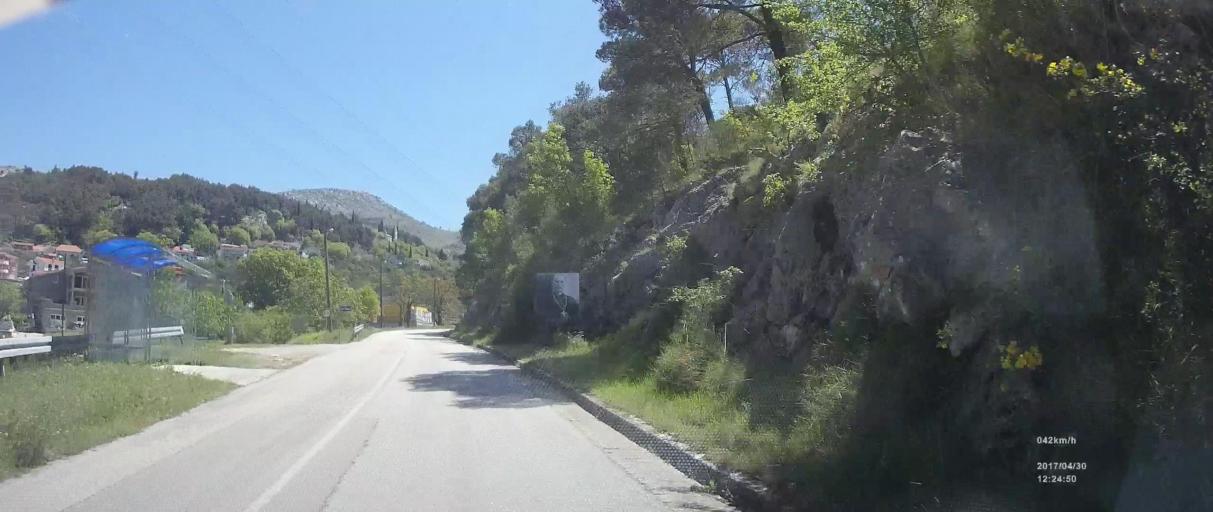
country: HR
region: Splitsko-Dalmatinska
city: Srinjine
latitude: 43.5096
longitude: 16.5884
